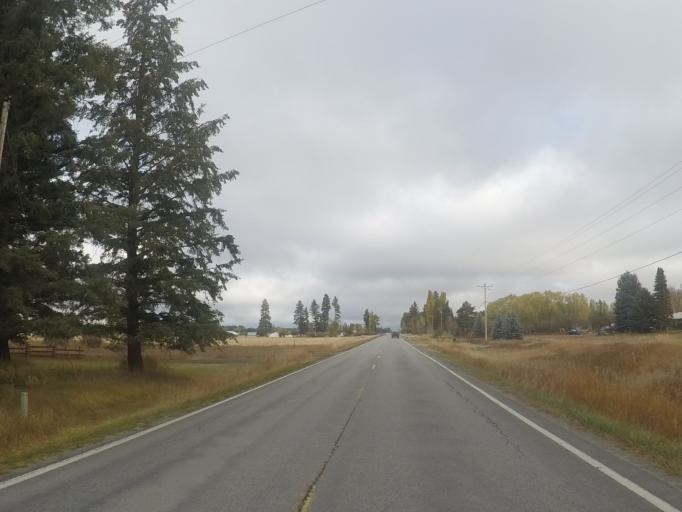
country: US
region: Montana
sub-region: Flathead County
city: Columbia Falls
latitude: 48.3156
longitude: -114.1594
